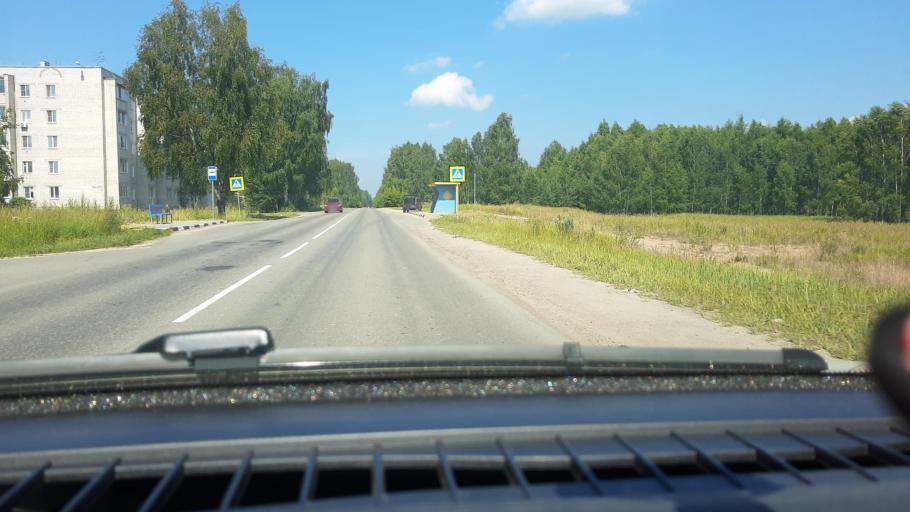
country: RU
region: Nizjnij Novgorod
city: Afonino
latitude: 56.3044
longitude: 44.1817
